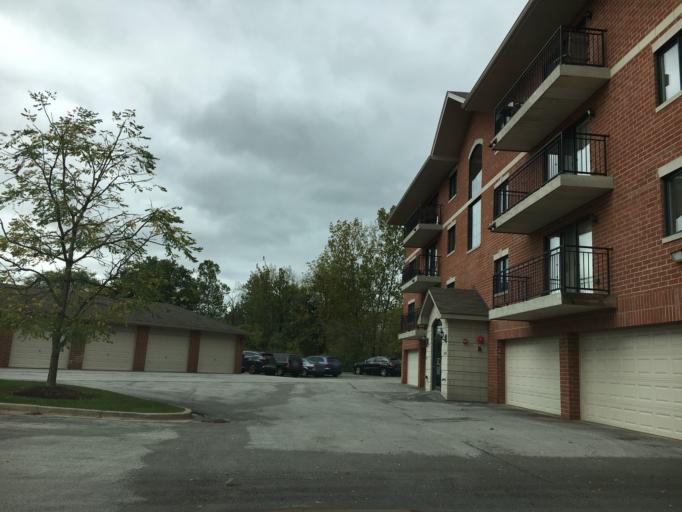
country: US
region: Illinois
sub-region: Cook County
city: Tinley Park
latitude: 41.6164
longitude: -87.7896
